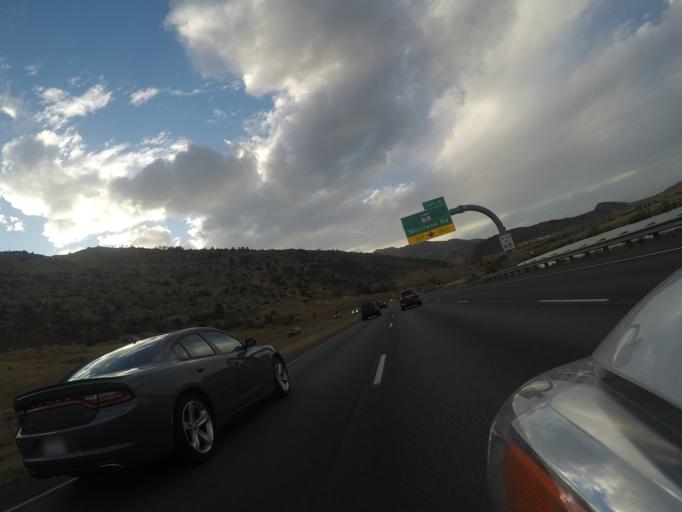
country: US
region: Colorado
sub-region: Jefferson County
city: Indian Hills
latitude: 39.6429
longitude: -105.1756
